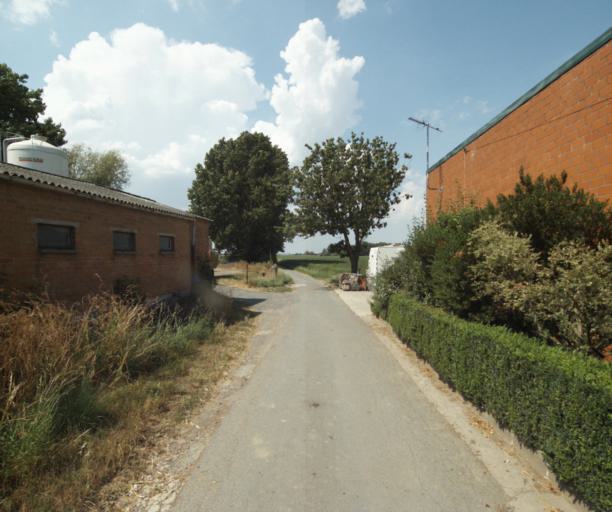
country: FR
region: Nord-Pas-de-Calais
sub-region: Departement du Nord
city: Quesnoy-sur-Deule
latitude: 50.7343
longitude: 3.0016
